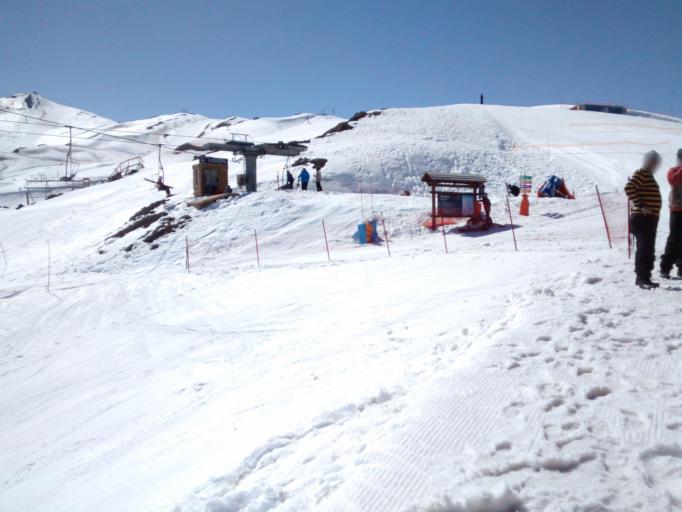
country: CL
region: Santiago Metropolitan
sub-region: Provincia de Santiago
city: Villa Presidente Frei, Nunoa, Santiago, Chile
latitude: -33.3529
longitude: -70.2491
